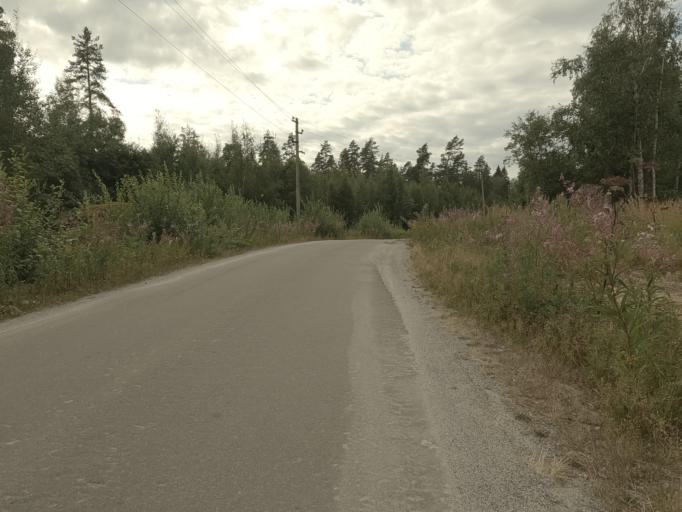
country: RU
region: Leningrad
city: Kamennogorsk
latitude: 60.9706
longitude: 29.1564
